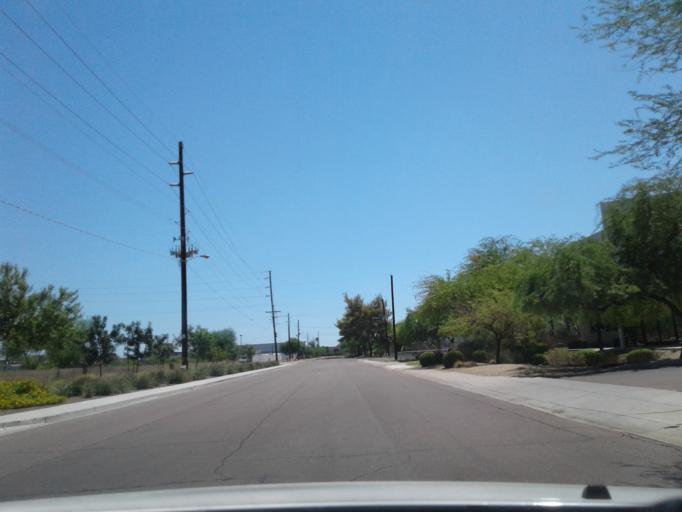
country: US
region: Arizona
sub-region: Maricopa County
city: Guadalupe
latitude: 33.4089
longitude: -112.0097
